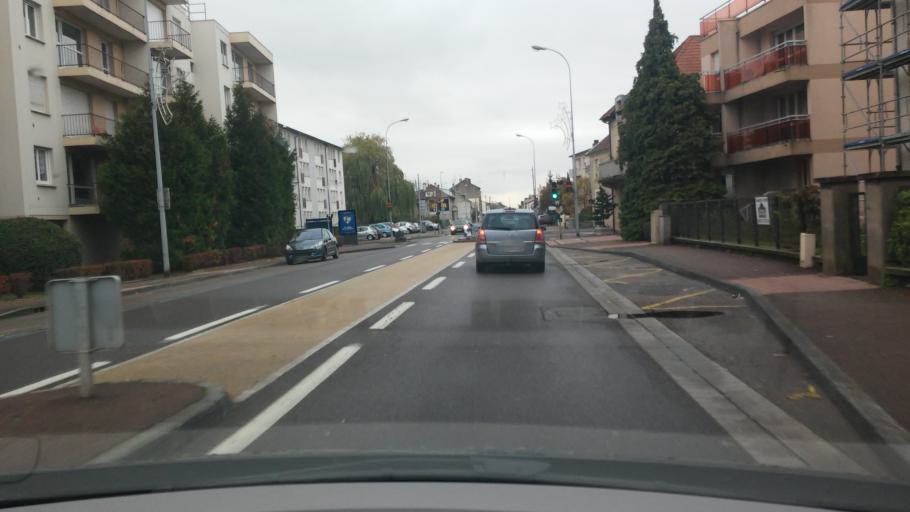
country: FR
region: Lorraine
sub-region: Departement de la Moselle
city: Hagondange
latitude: 49.2544
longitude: 6.1699
